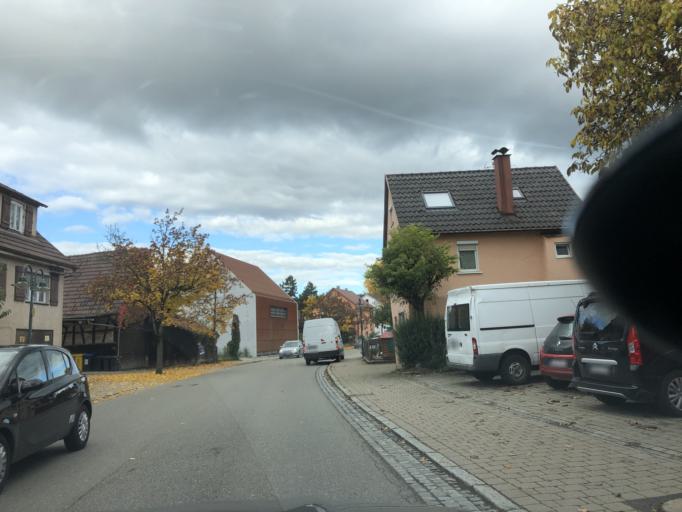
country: DE
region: Baden-Wuerttemberg
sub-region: Regierungsbezirk Stuttgart
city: Winterbach
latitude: 48.8004
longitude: 9.4791
